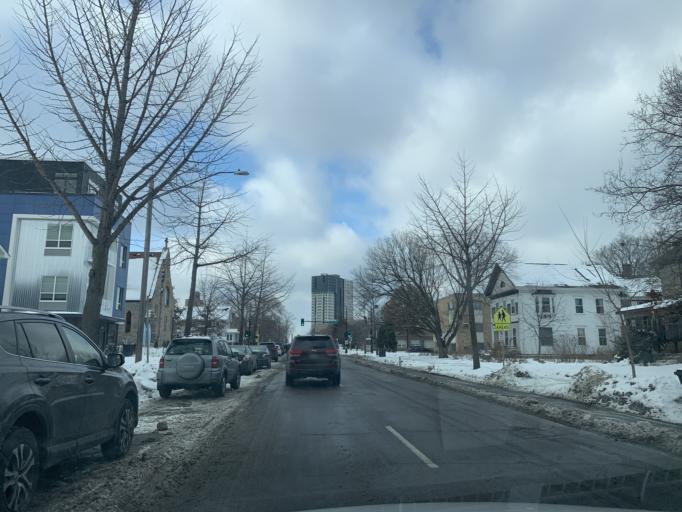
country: US
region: Minnesota
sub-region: Hennepin County
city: Minneapolis
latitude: 44.9857
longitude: -93.2489
